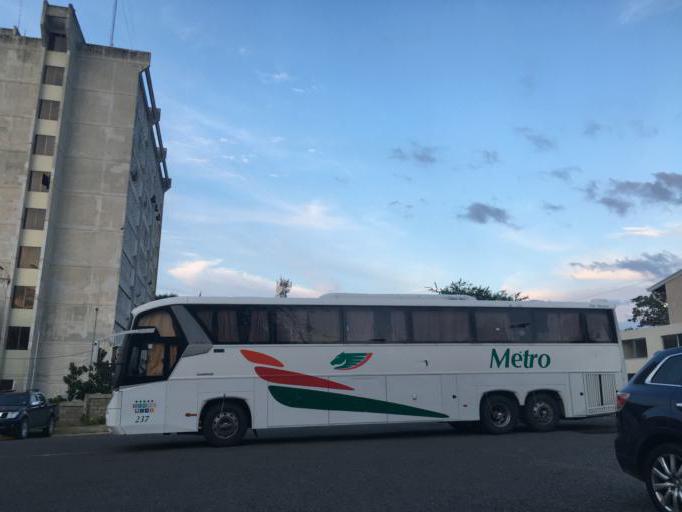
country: DO
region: Santiago
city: Santiago de los Caballeros
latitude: 19.4595
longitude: -70.6871
